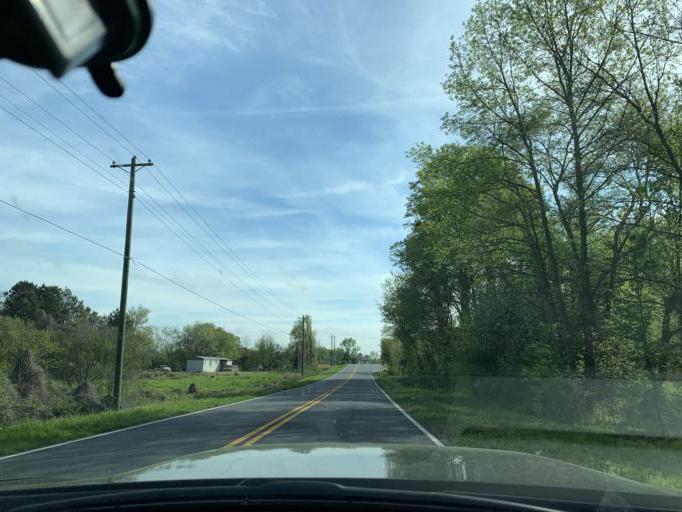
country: US
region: Georgia
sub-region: Forsyth County
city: Cumming
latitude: 34.2550
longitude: -84.1416
